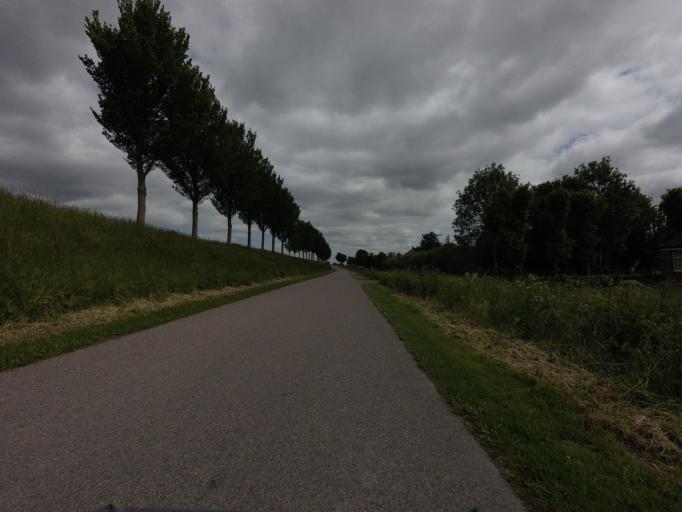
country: NL
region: North Holland
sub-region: Gemeente Beemster
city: Halfweg
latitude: 52.5522
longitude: 4.8505
